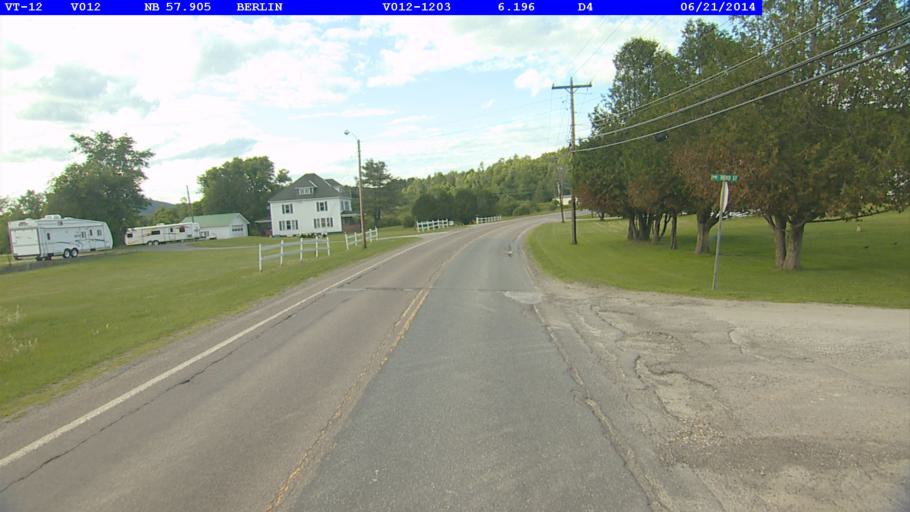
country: US
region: Vermont
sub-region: Washington County
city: Montpelier
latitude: 44.2422
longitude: -72.5948
